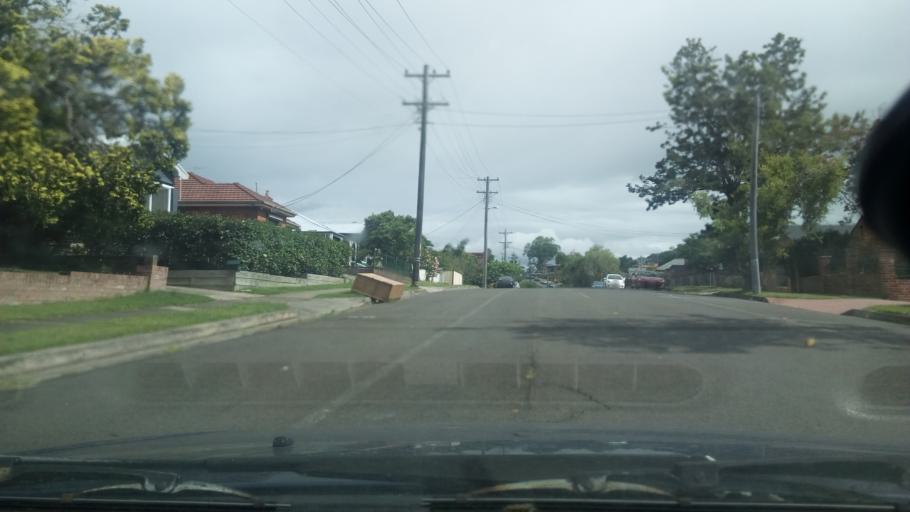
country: AU
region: New South Wales
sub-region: Wollongong
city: Keiraville
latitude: -34.4225
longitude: 150.8750
